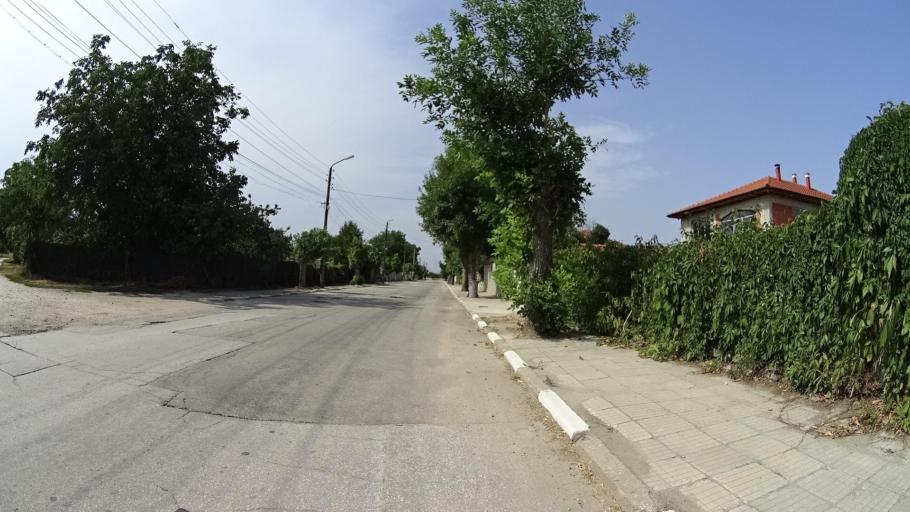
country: BG
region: Plovdiv
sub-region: Obshtina Kaloyanovo
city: Kaloyanovo
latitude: 42.2645
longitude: 24.8007
